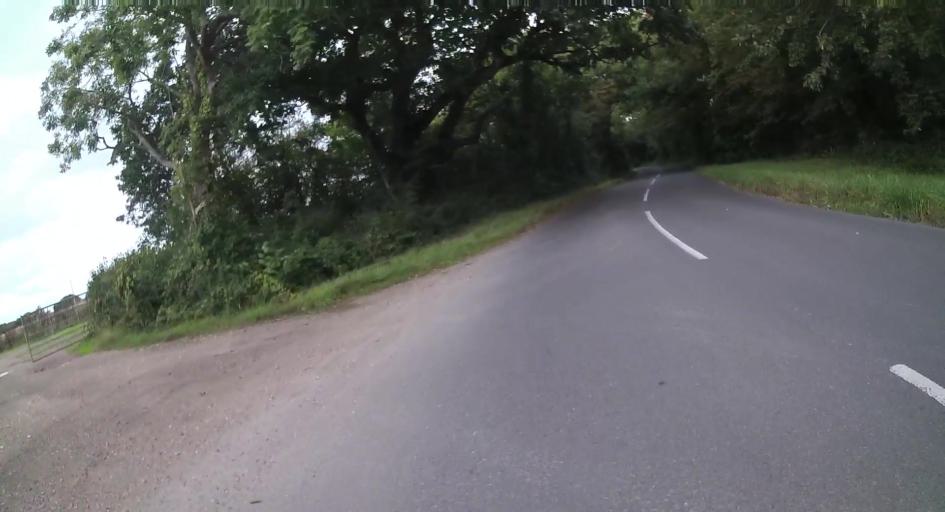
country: GB
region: England
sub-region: Isle of Wight
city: Freshwater
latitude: 50.6818
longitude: -1.4958
